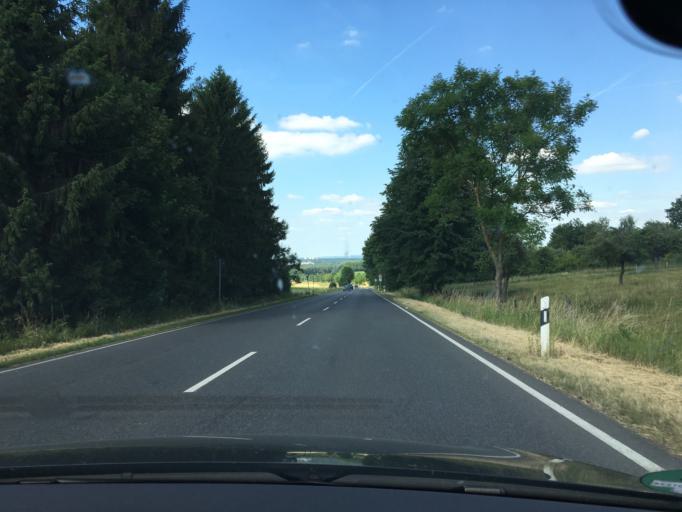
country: DE
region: North Rhine-Westphalia
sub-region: Regierungsbezirk Koln
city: Kreuzau
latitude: 50.7400
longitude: 6.4589
